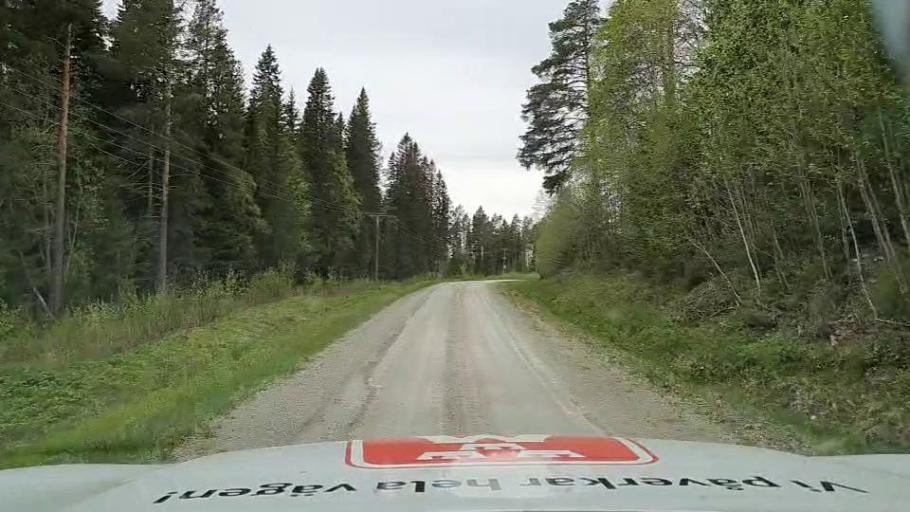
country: SE
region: Jaemtland
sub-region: Bergs Kommun
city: Hoverberg
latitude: 62.6701
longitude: 14.8087
